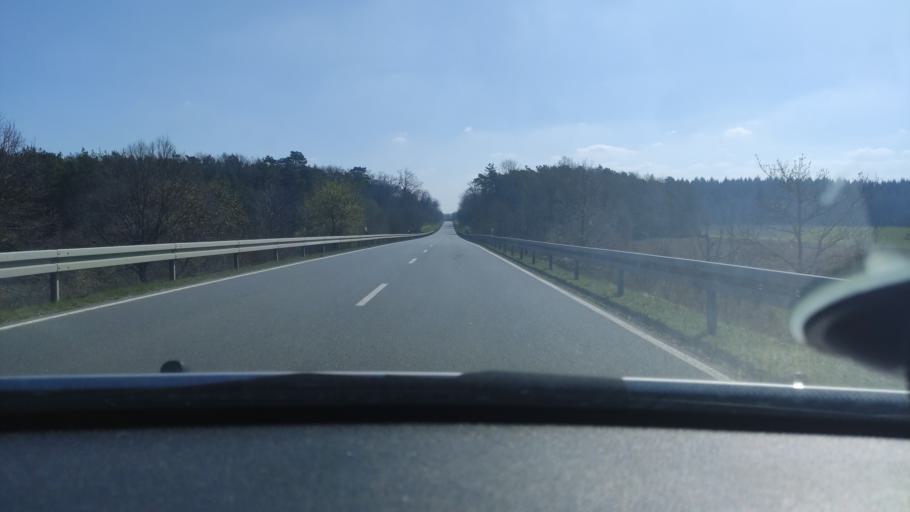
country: DE
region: Baden-Wuerttemberg
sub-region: Regierungsbezirk Stuttgart
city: Boxberg
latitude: 49.4643
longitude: 9.5885
